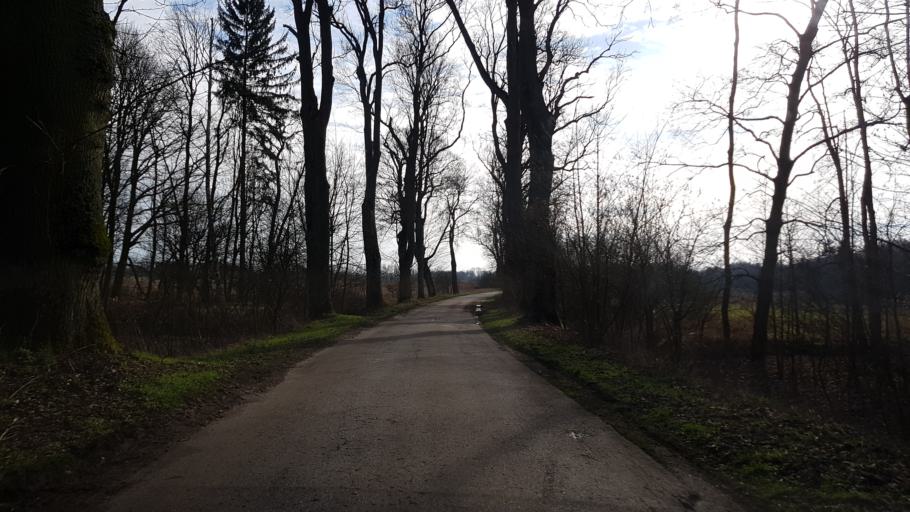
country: PL
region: West Pomeranian Voivodeship
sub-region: Powiat policki
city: Dobra
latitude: 53.5656
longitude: 14.3195
